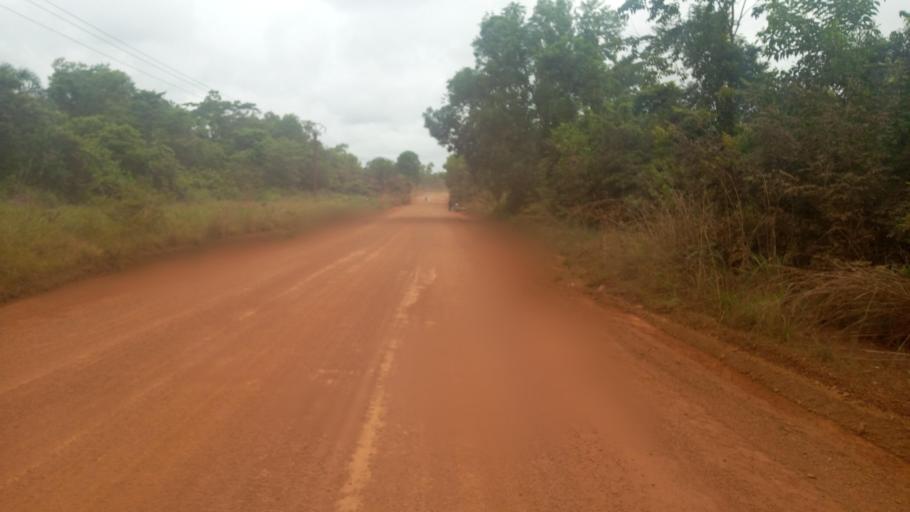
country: SL
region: Southern Province
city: Mogbwemo
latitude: 7.7458
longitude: -12.2917
